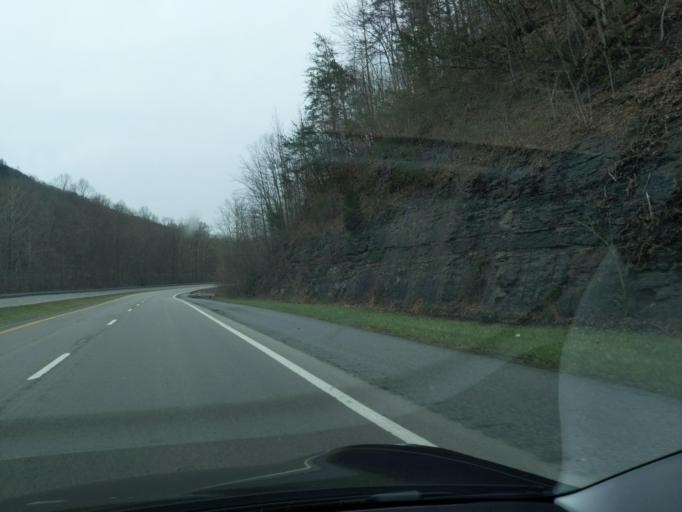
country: US
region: Kentucky
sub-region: Bell County
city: Pineville
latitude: 36.6875
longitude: -83.6846
